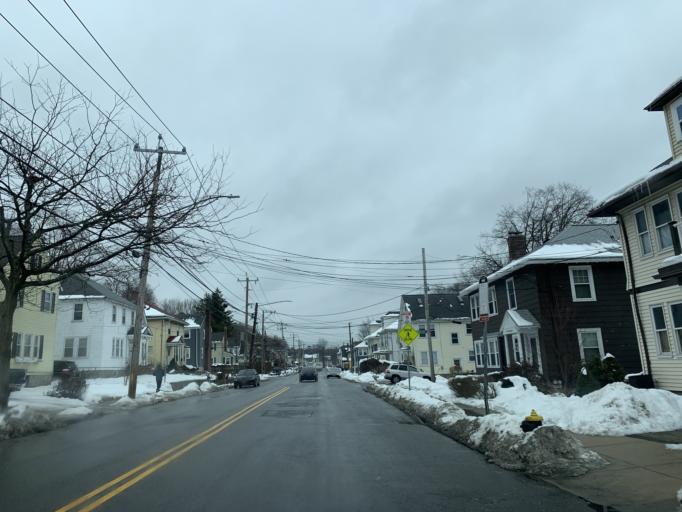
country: US
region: Massachusetts
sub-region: Norfolk County
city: Dedham
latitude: 42.2860
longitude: -71.1640
